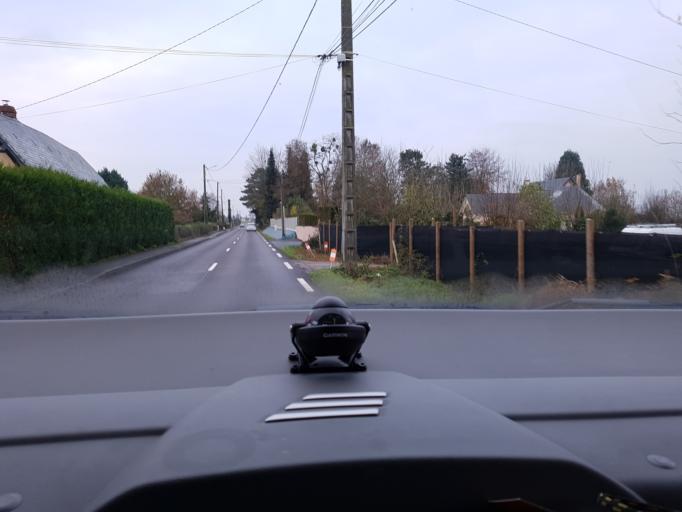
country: FR
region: Haute-Normandie
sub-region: Departement de la Seine-Maritime
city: Saint-Pierre-de-Varengeville
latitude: 49.5000
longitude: 0.9506
